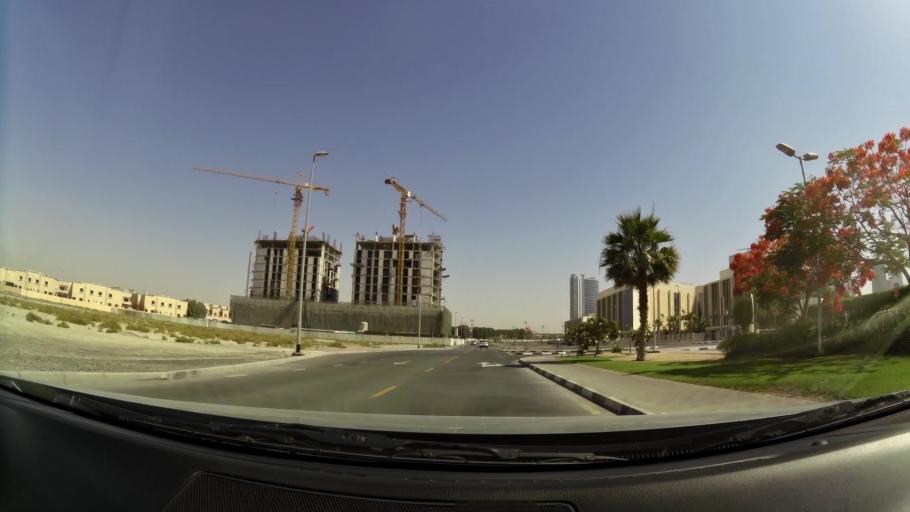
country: AE
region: Dubai
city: Dubai
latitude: 25.1061
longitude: 55.1817
